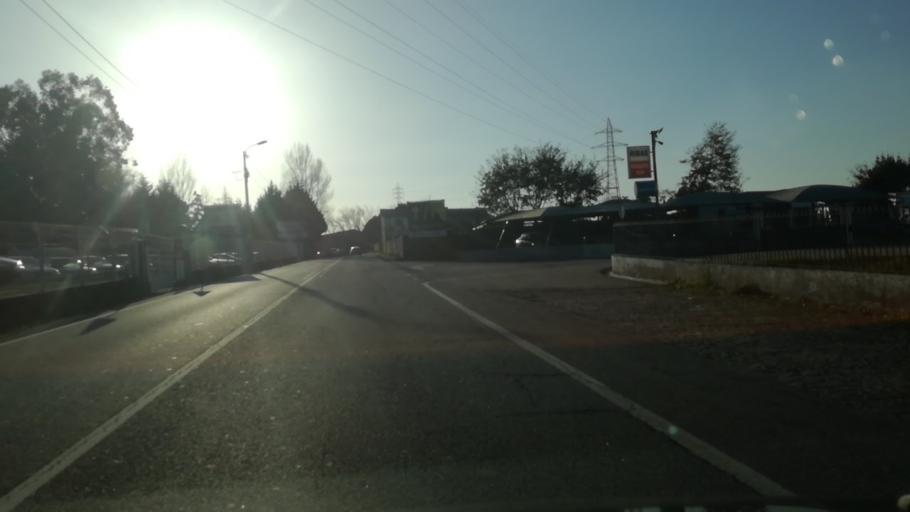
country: PT
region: Braga
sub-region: Vila Nova de Famalicao
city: Ferreiros
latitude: 41.3571
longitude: -8.5506
